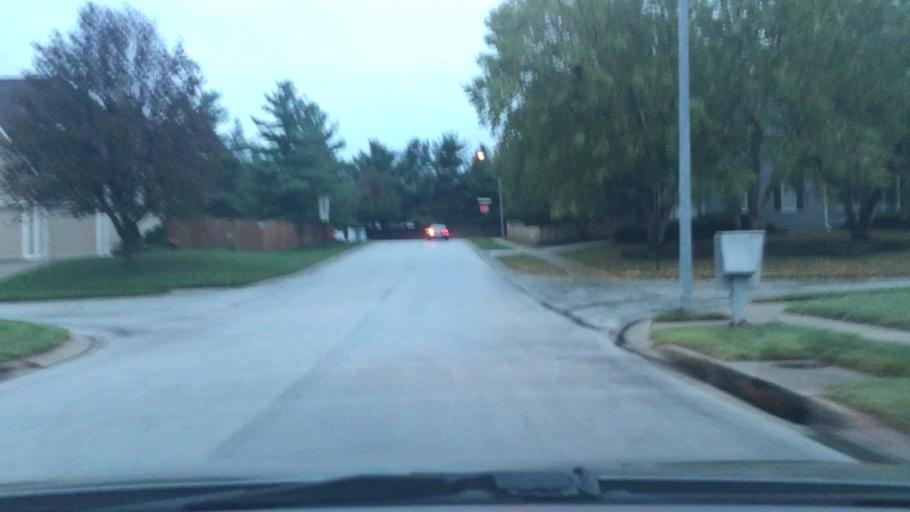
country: US
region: Missouri
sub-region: Jackson County
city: Lees Summit
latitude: 38.9881
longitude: -94.3630
